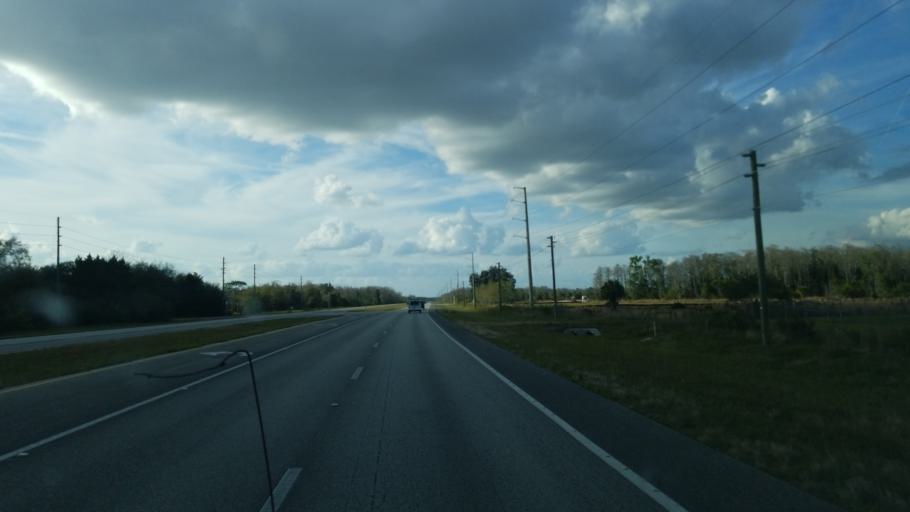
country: US
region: Florida
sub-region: Osceola County
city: Saint Cloud
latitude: 28.1528
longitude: -81.1056
